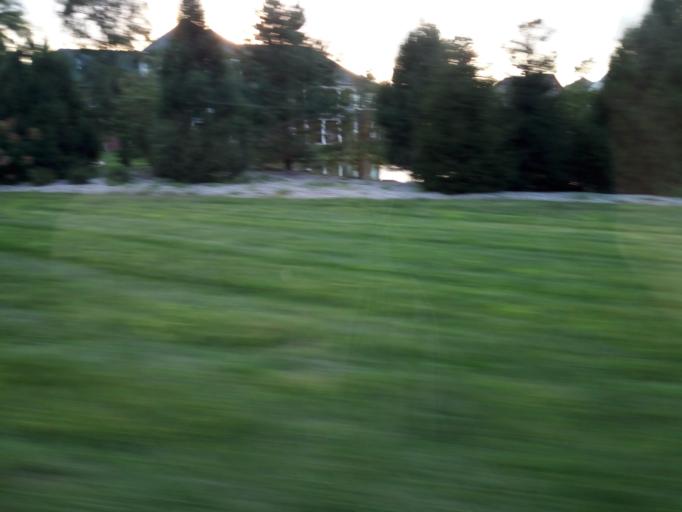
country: US
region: Kentucky
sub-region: Oldham County
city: Pewee Valley
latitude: 38.2763
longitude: -85.4891
